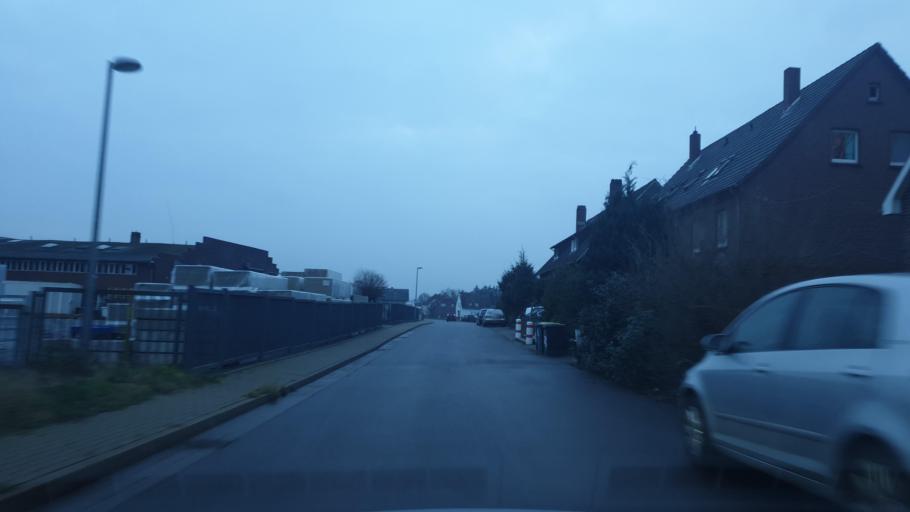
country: DE
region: North Rhine-Westphalia
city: Bad Oeynhausen
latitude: 52.2378
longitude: 8.8342
